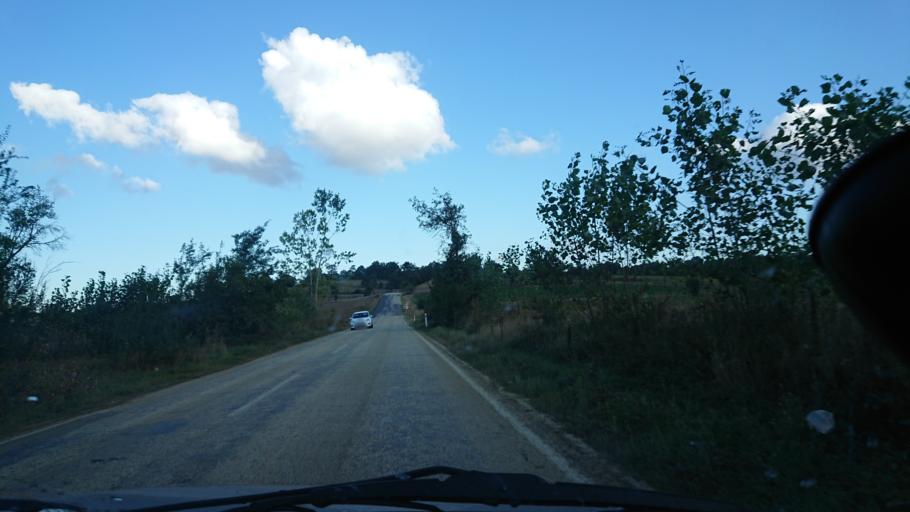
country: TR
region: Bilecik
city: Pazaryeri
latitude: 40.0091
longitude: 29.8640
